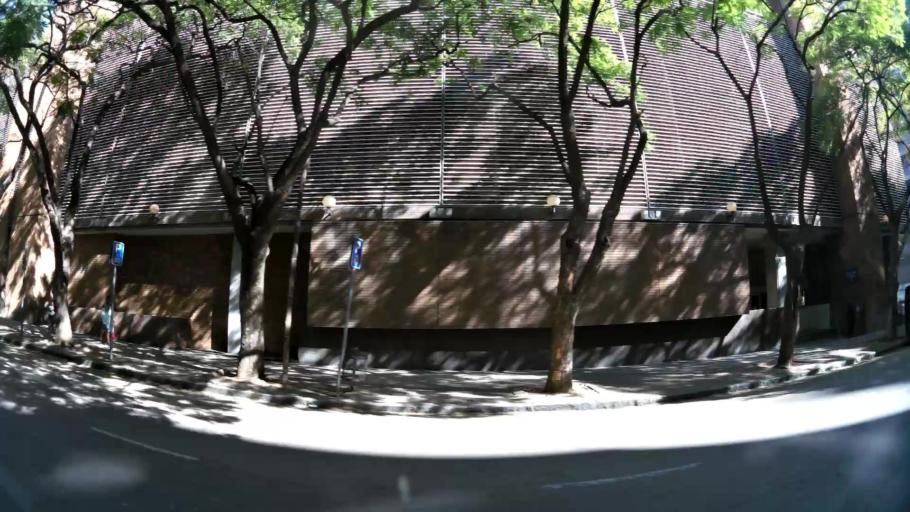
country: ZA
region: Gauteng
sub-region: City of Tshwane Metropolitan Municipality
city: Pretoria
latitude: -25.7484
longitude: 28.1857
